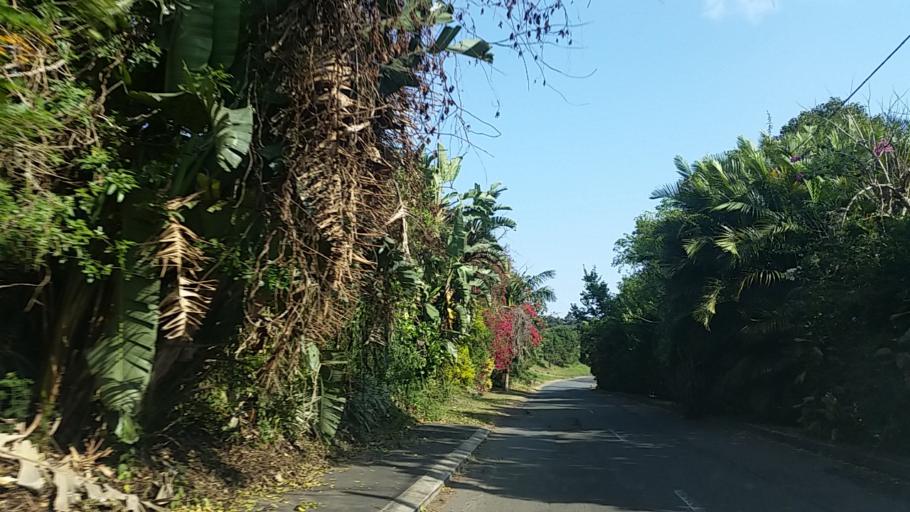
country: ZA
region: KwaZulu-Natal
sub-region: eThekwini Metropolitan Municipality
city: Berea
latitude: -29.8354
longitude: 30.9054
